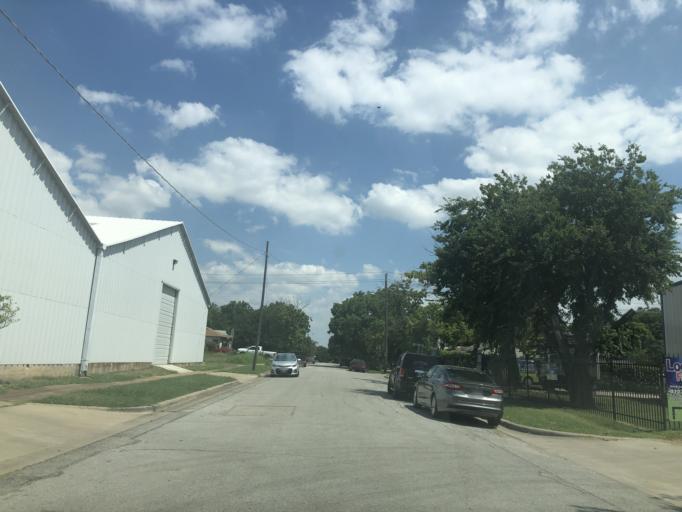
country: US
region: Texas
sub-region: Dallas County
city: Grand Prairie
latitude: 32.7421
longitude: -97.0241
